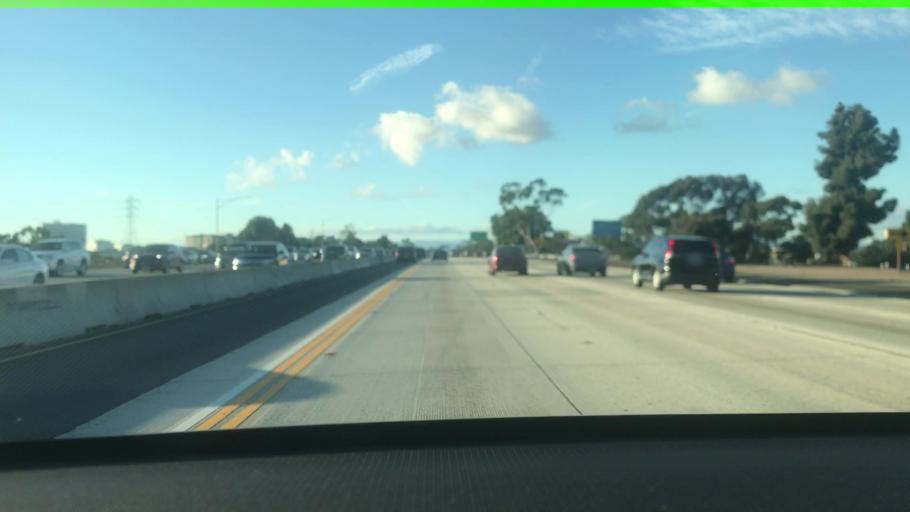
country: US
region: California
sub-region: Los Angeles County
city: Lawndale
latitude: 33.8895
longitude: -118.3593
